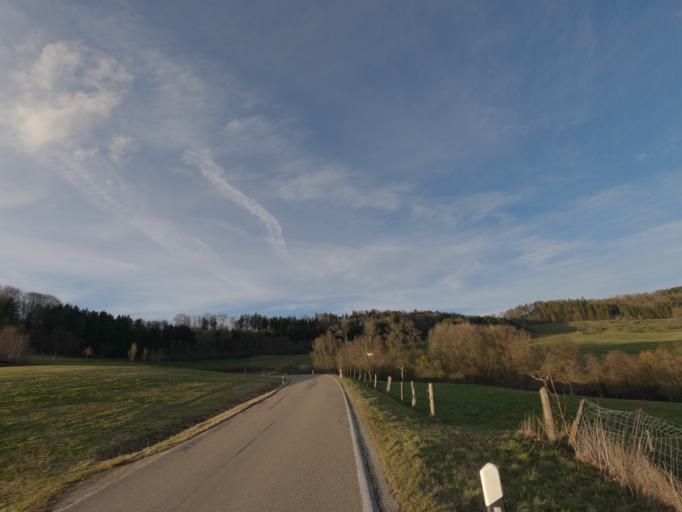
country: DE
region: Baden-Wuerttemberg
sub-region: Regierungsbezirk Stuttgart
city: Ottenbach
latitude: 48.7455
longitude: 9.7517
